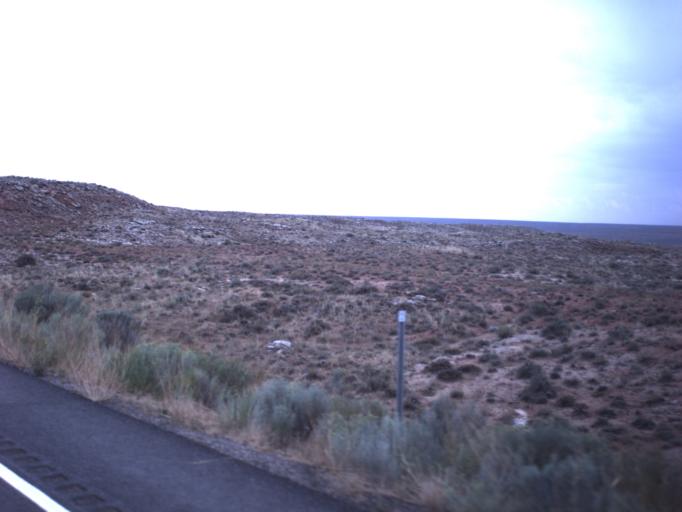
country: US
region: Utah
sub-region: Uintah County
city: Naples
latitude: 40.2658
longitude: -109.4535
